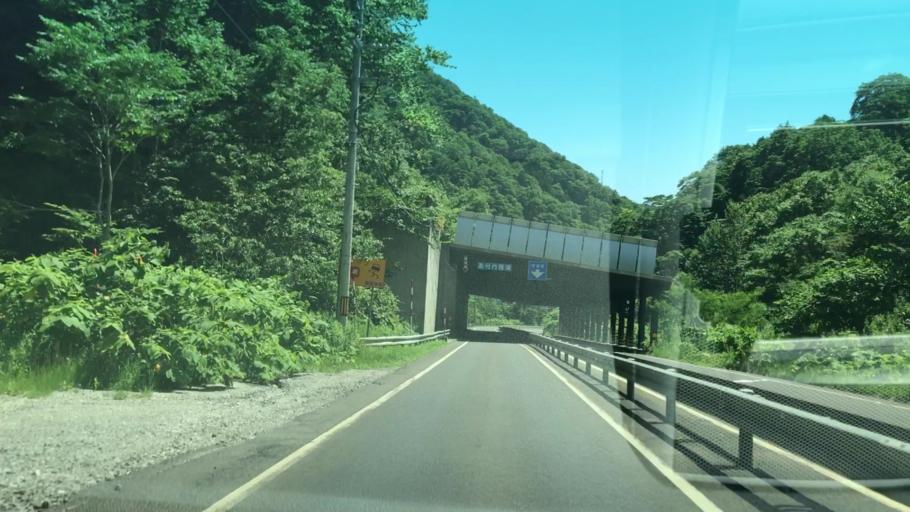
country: JP
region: Hokkaido
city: Yoichi
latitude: 43.0466
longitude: 140.6811
